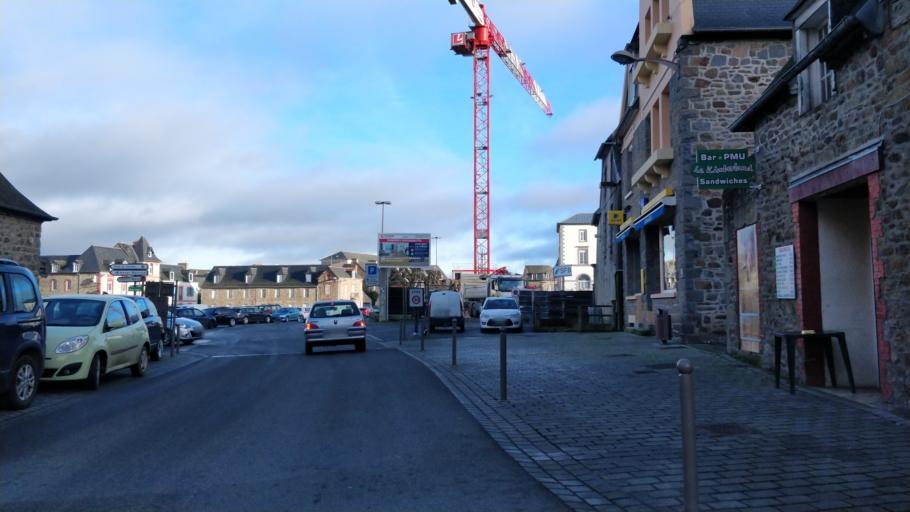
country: FR
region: Brittany
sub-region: Departement des Cotes-d'Armor
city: Lamballe
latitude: 48.4698
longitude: -2.5168
